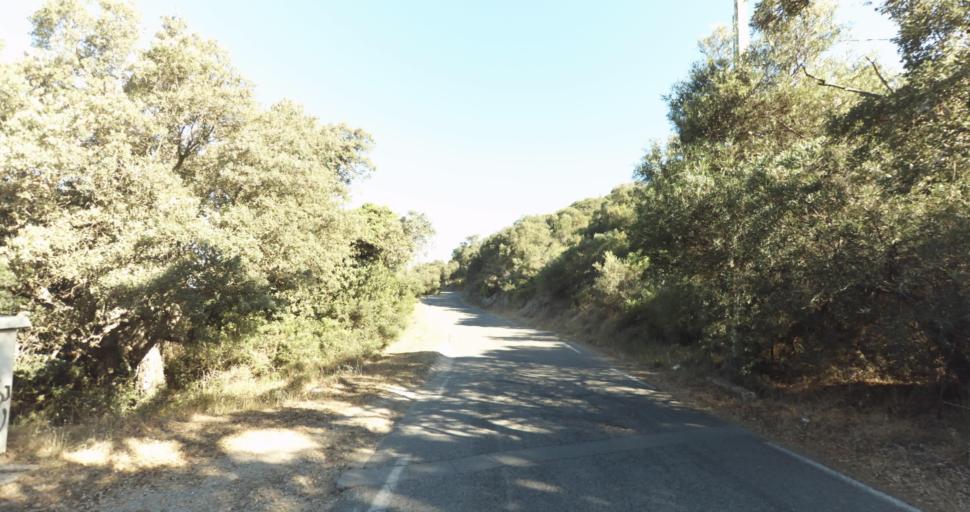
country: FR
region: Provence-Alpes-Cote d'Azur
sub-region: Departement du Var
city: Ramatuelle
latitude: 43.2159
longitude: 6.6016
